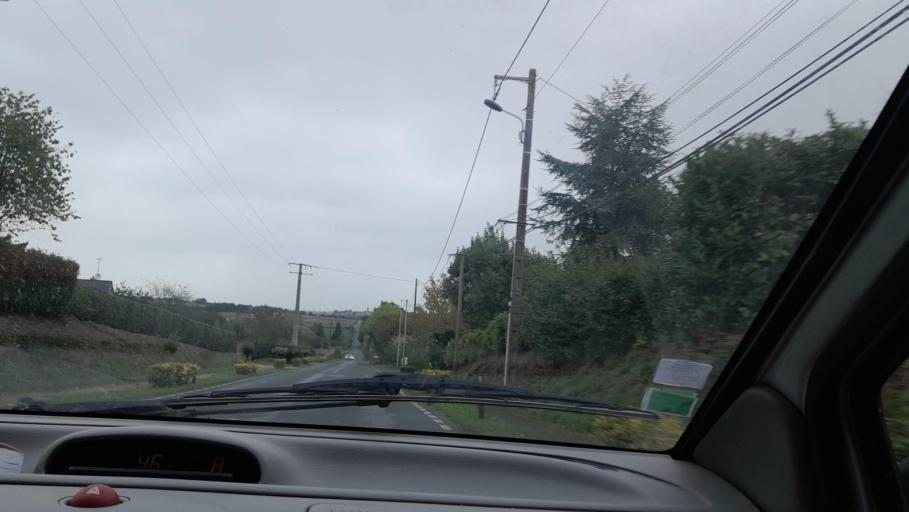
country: FR
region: Pays de la Loire
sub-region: Departement de Maine-et-Loire
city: Pouance
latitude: 47.7173
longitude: -1.1779
